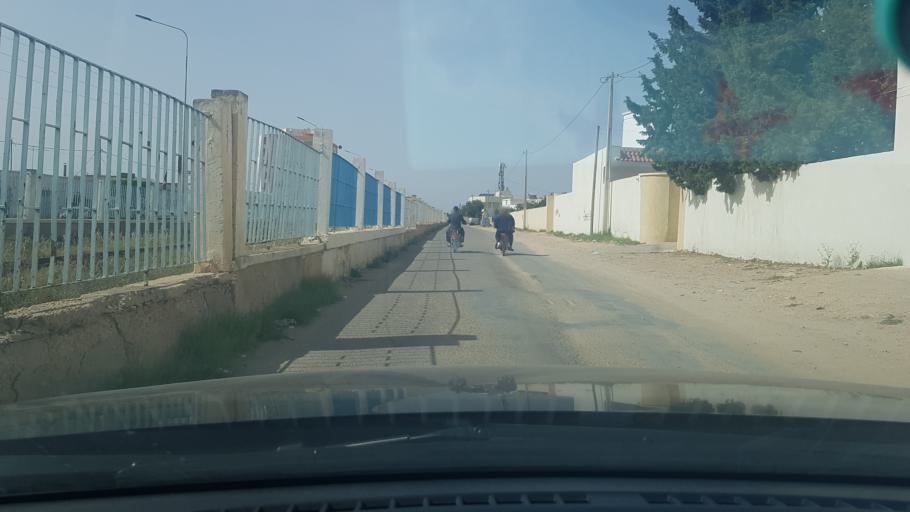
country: TN
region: Safaqis
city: Al Qarmadah
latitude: 34.8064
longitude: 10.7618
